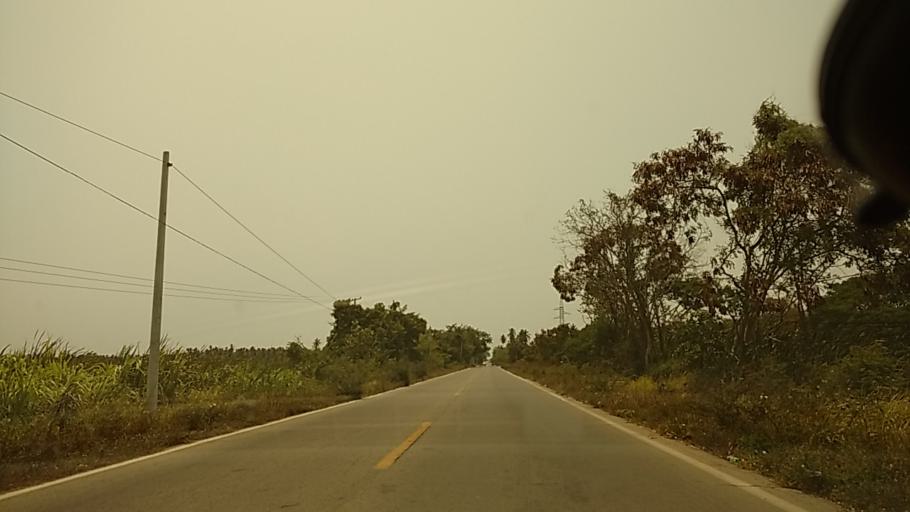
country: MX
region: Guerrero
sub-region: Tecpan de Galeana
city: Villa Rotaria
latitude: 17.2714
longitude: -100.9013
